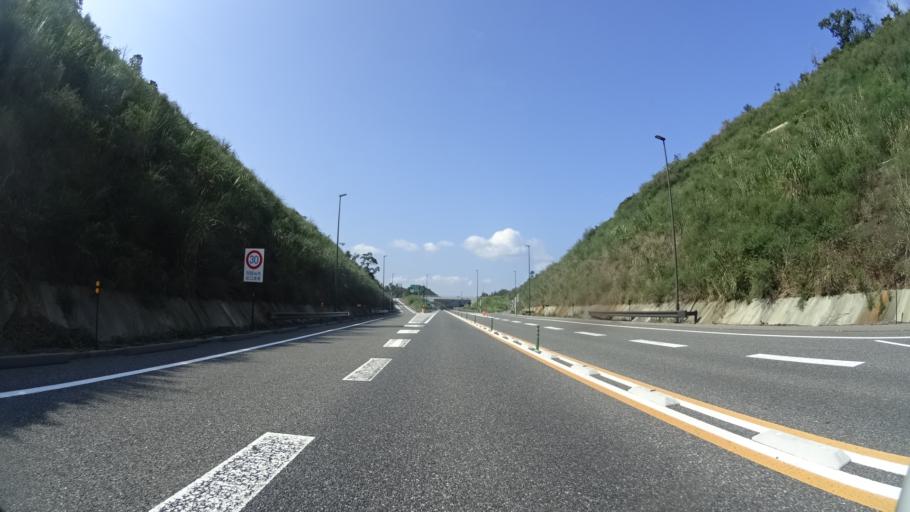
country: JP
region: Shimane
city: Gotsucho
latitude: 35.0844
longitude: 132.3466
